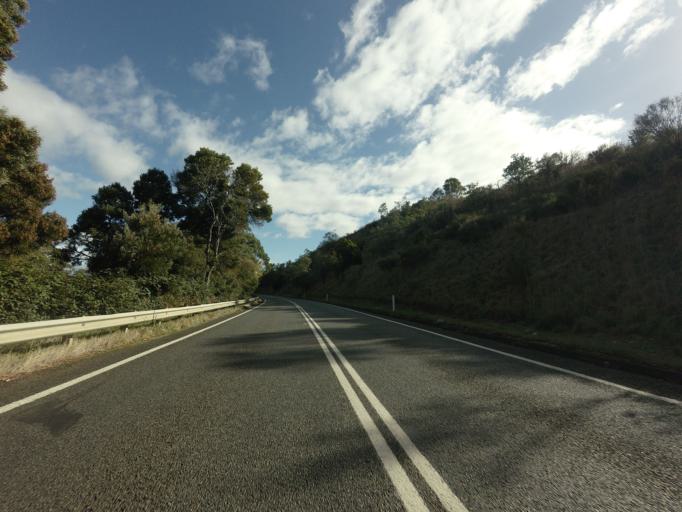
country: AU
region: Tasmania
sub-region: Derwent Valley
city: New Norfolk
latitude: -42.7277
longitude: 146.9557
